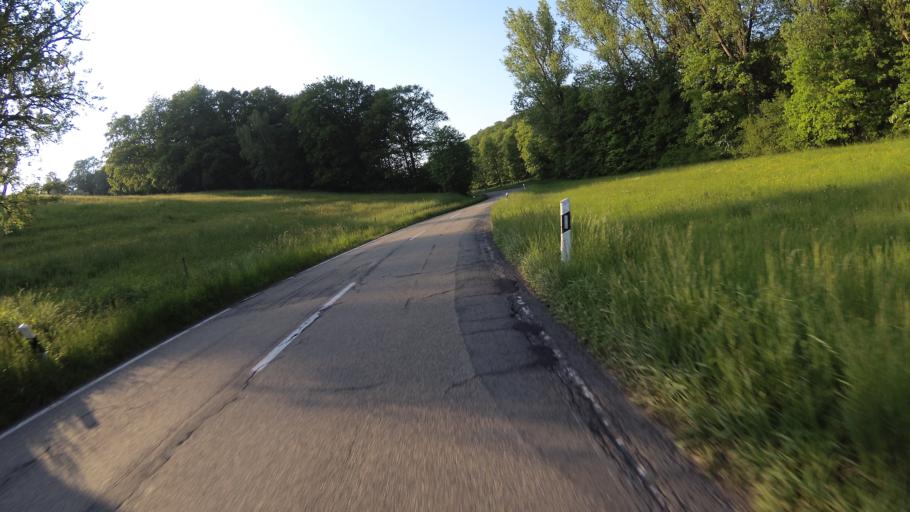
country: DE
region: Rheinland-Pfalz
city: Dietrichingen
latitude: 49.2113
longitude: 7.4242
